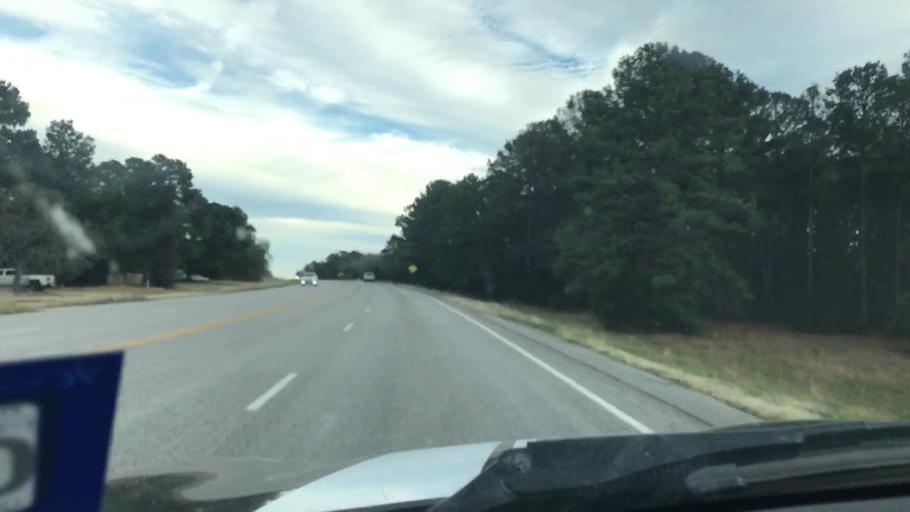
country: US
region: Texas
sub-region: Bastrop County
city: Camp Swift
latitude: 30.2415
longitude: -97.2133
